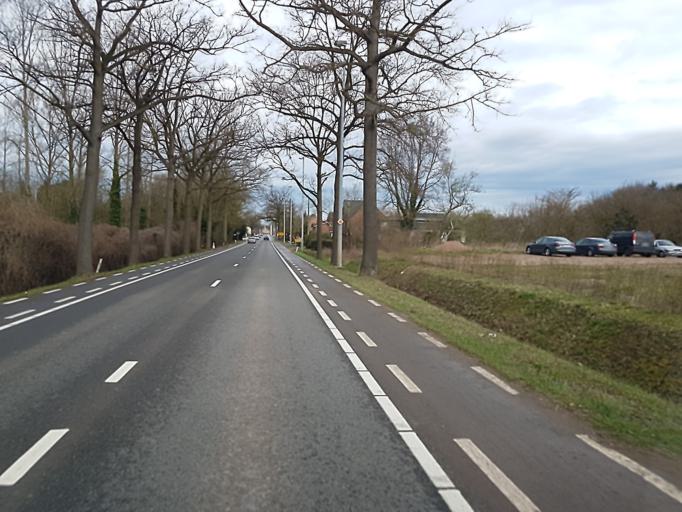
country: BE
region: Flanders
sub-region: Provincie Limburg
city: Kortessem
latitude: 50.8779
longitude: 5.3605
